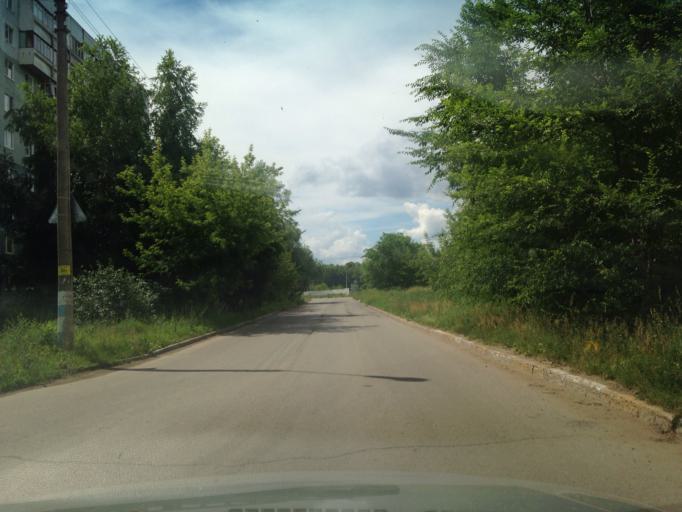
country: RU
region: Ulyanovsk
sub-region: Ulyanovskiy Rayon
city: Ulyanovsk
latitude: 54.3247
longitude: 48.4710
